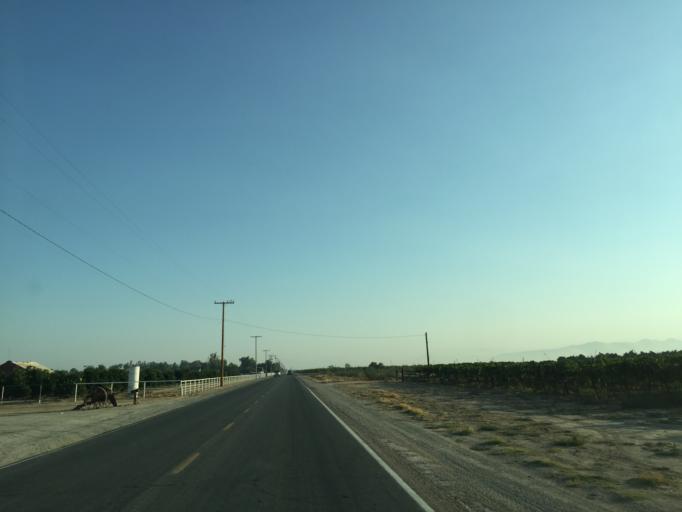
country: US
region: California
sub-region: Tulare County
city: Ivanhoe
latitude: 36.4173
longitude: -119.2781
